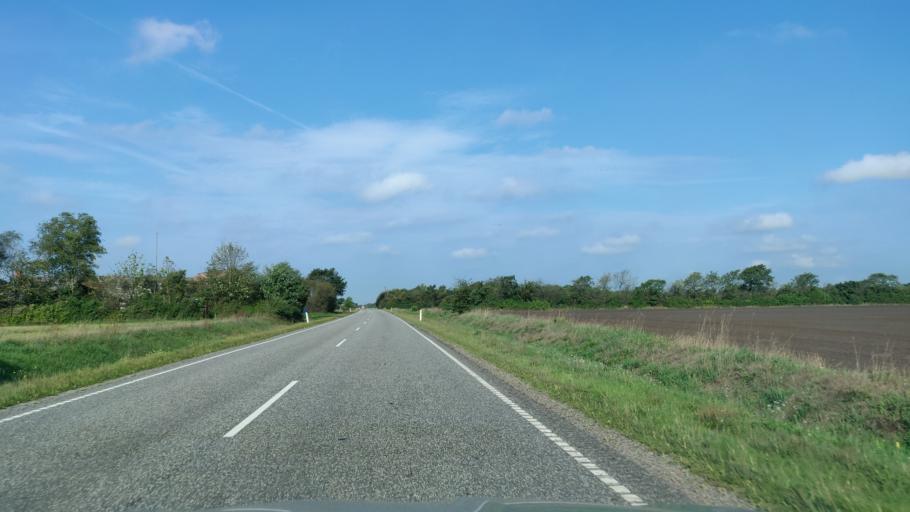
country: DK
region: Central Jutland
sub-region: Herning Kommune
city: Sunds
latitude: 56.2555
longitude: 9.0453
